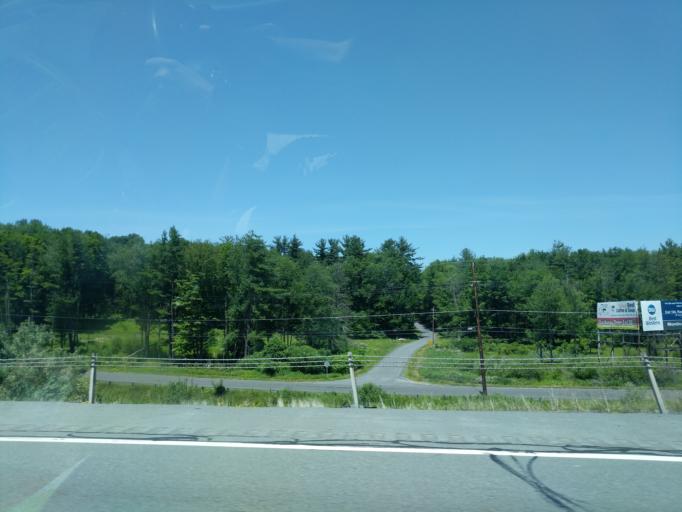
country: US
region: New York
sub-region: Sullivan County
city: Rock Hill
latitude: 41.6400
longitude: -74.6346
